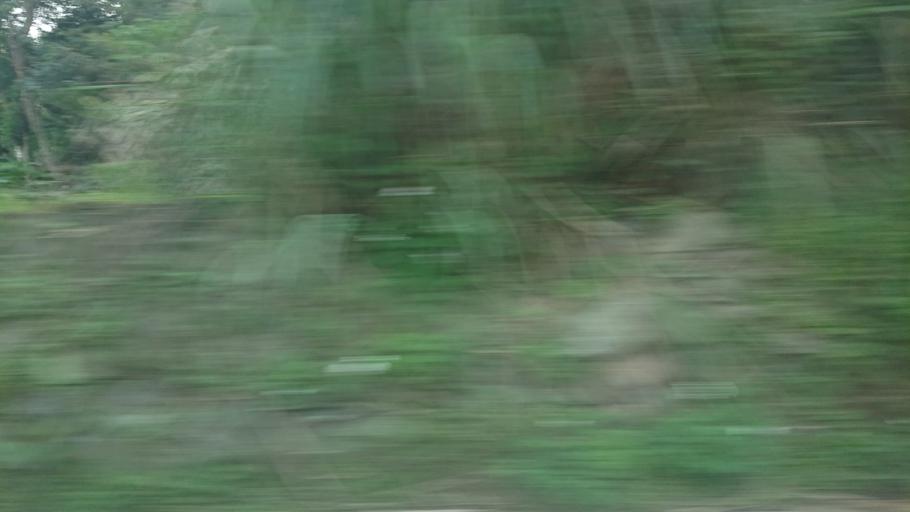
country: TW
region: Taiwan
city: Daxi
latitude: 24.8932
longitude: 121.3756
